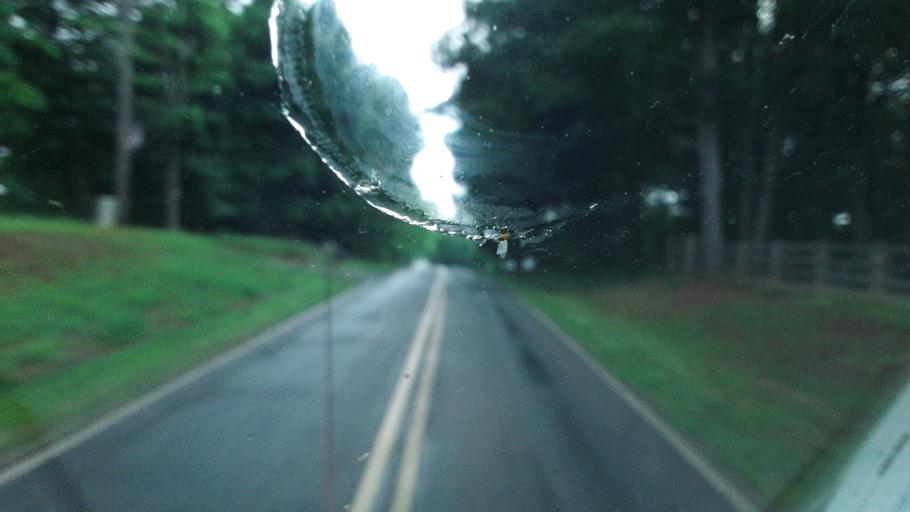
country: US
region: North Carolina
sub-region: Yadkin County
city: Jonesville
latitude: 36.1061
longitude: -80.8963
